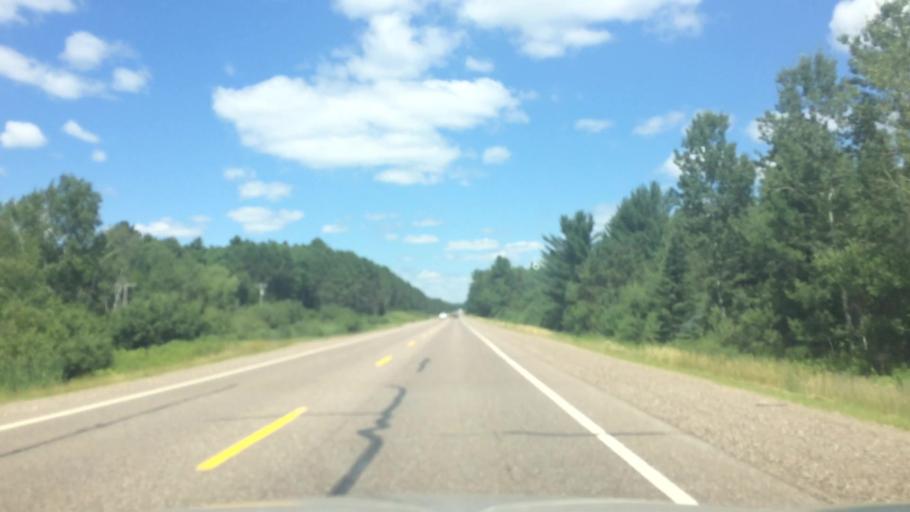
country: US
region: Wisconsin
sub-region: Vilas County
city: Lac du Flambeau
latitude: 45.9569
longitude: -89.7005
